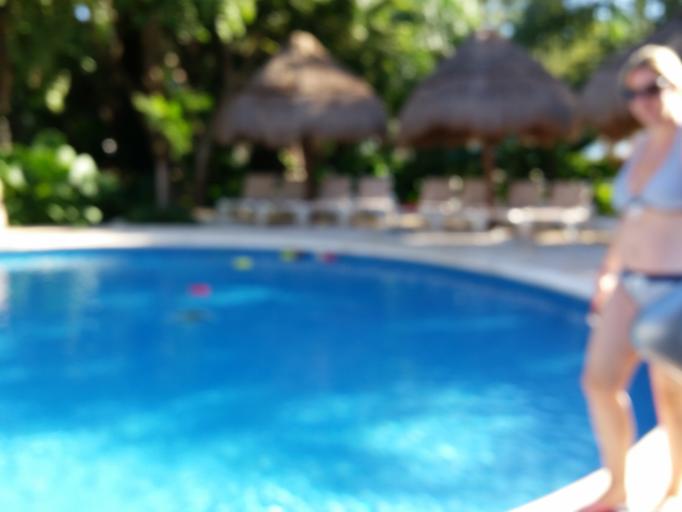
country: MX
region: Quintana Roo
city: Playa del Carmen
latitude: 20.6700
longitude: -87.0316
